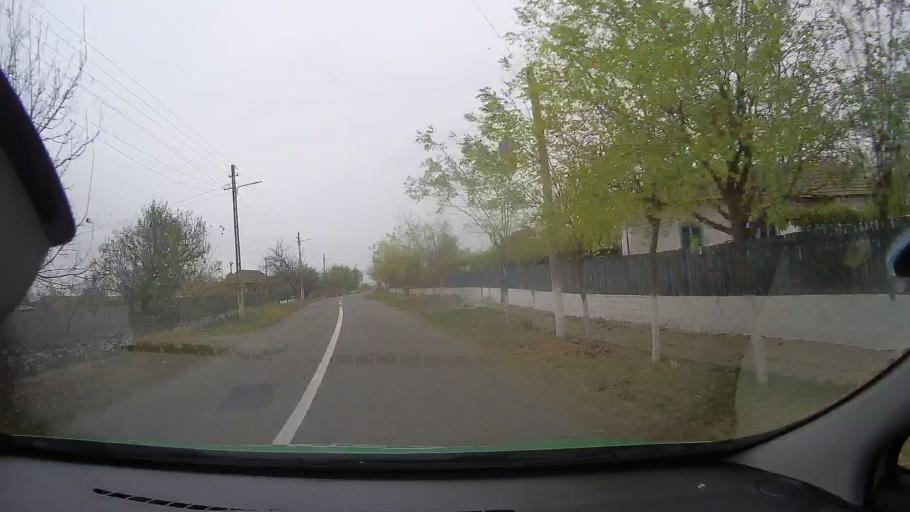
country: RO
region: Constanta
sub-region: Comuna Vulturu
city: Vulturu
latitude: 44.7069
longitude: 28.2342
